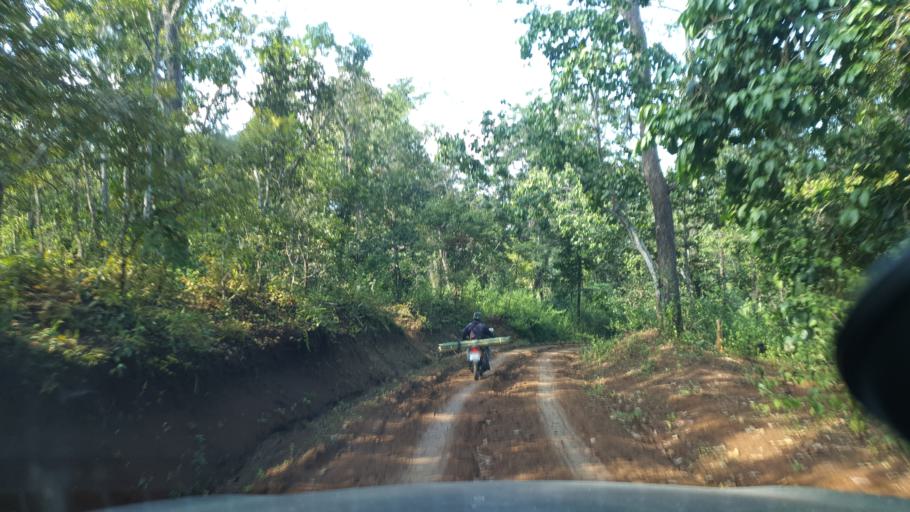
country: TH
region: Chiang Mai
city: Wiang Haeng
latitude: 19.3634
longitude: 98.7167
